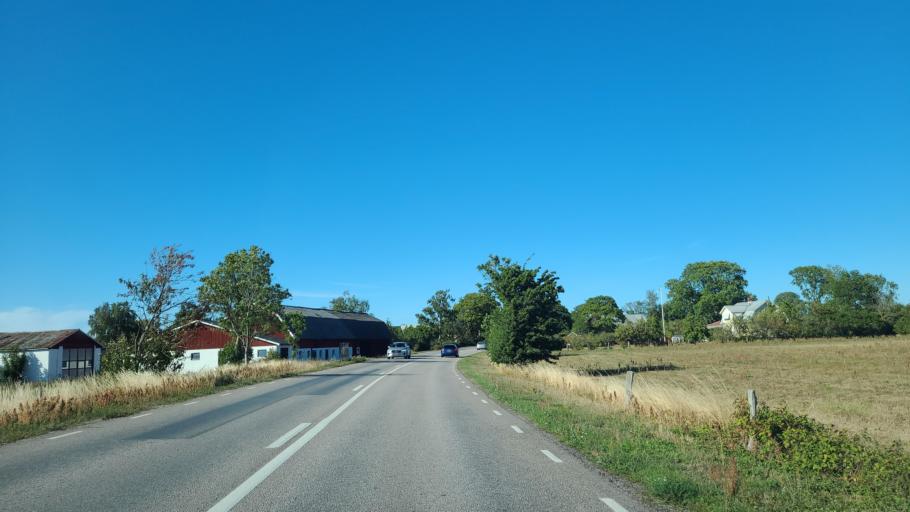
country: SE
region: Kalmar
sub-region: Borgholms Kommun
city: Borgholm
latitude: 57.2325
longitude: 17.0530
